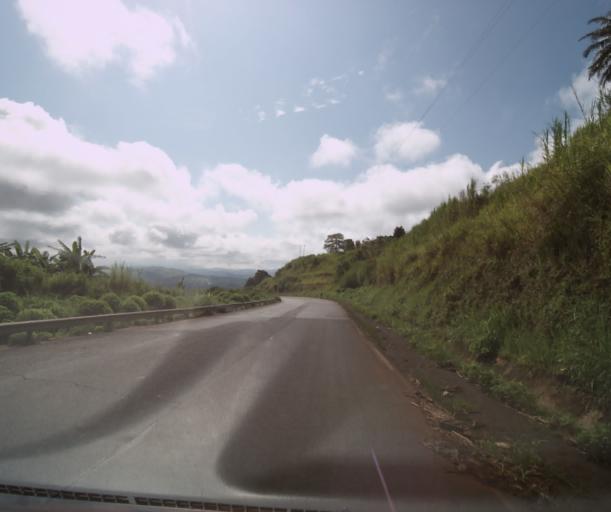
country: CM
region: West
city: Bafoussam
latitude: 5.4829
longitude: 10.4888
